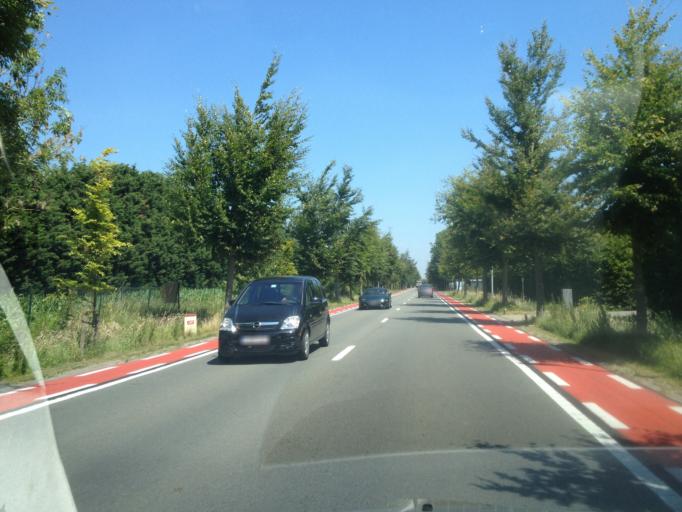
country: BE
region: Flanders
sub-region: Provincie West-Vlaanderen
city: Jabbeke
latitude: 51.1751
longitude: 3.0690
